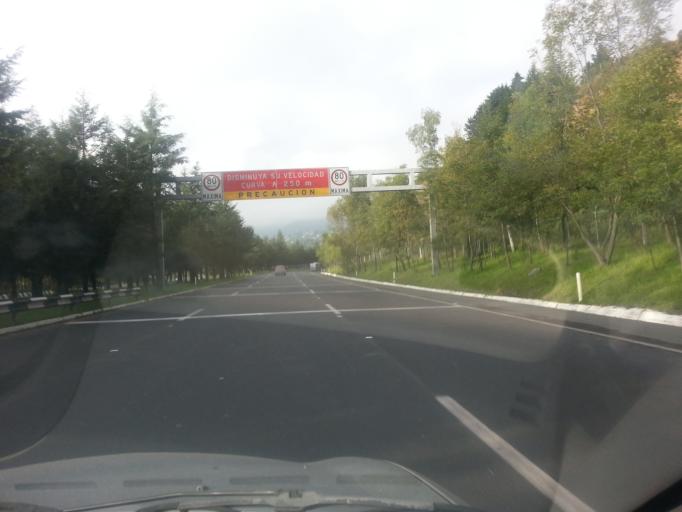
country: MX
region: Mexico City
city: Cuajimalpa
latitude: 19.3515
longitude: -99.2801
